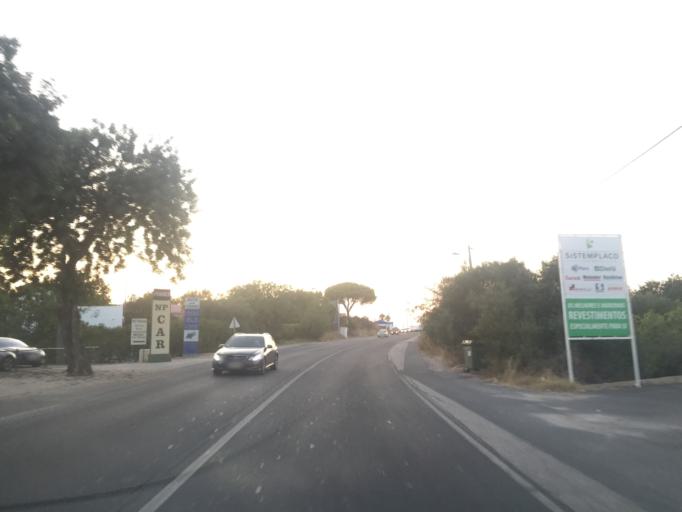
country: PT
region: Faro
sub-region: Faro
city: Santa Barbara de Nexe
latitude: 37.0775
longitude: -7.9894
